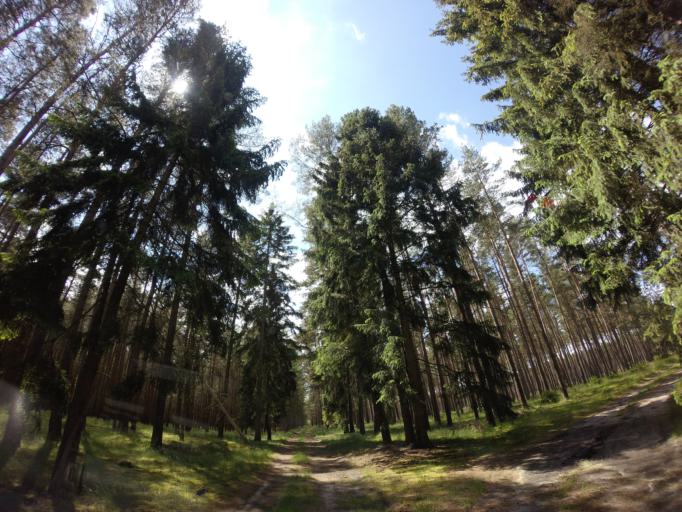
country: PL
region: West Pomeranian Voivodeship
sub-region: Powiat drawski
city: Kalisz Pomorski
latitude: 53.1836
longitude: 15.9391
